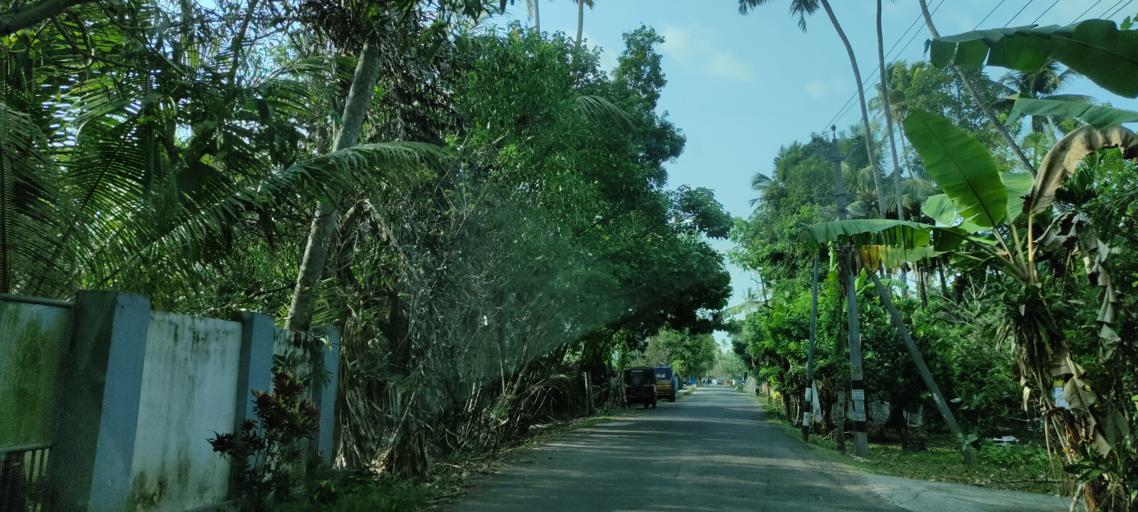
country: IN
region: Kerala
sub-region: Alappuzha
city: Vayalar
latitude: 9.7181
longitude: 76.2876
